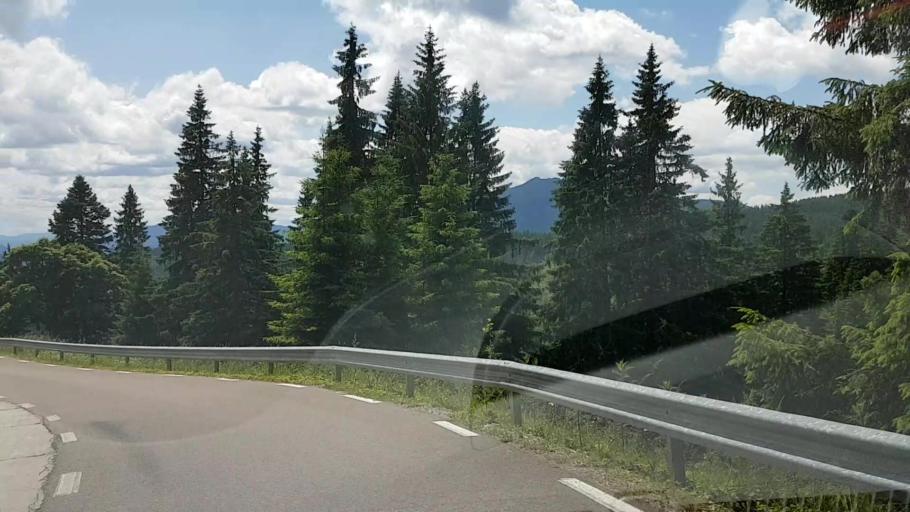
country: RO
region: Suceava
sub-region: Municipiul Campulung Moldovenesc
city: Campulung Moldovenesc
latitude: 47.4380
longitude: 25.5588
